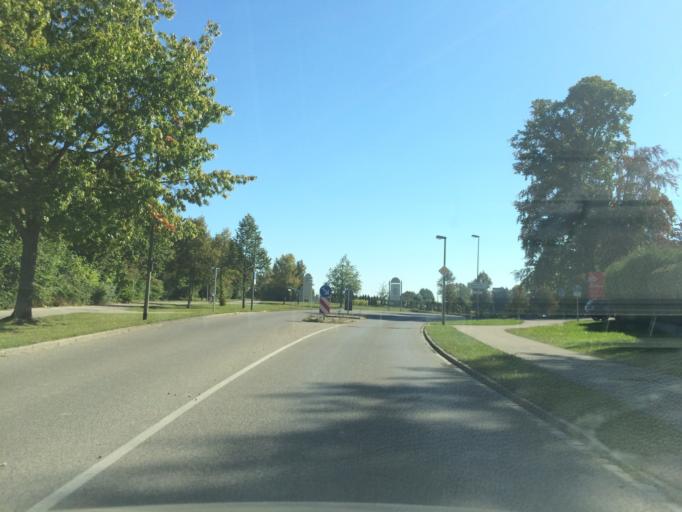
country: DE
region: Bavaria
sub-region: Swabia
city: Friedberg
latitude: 48.3492
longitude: 10.9924
